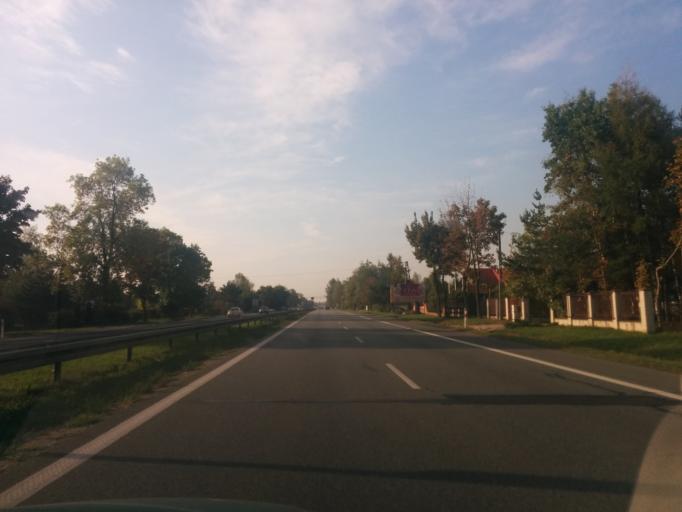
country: PL
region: Masovian Voivodeship
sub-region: Powiat piaseczynski
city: Tarczyn
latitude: 52.0442
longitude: 20.8633
